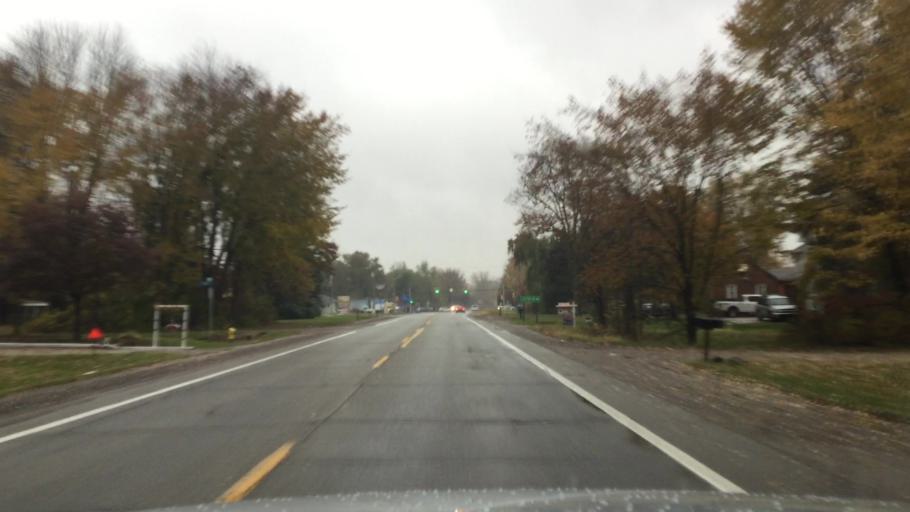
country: US
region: Michigan
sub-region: Macomb County
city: New Baltimore
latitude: 42.6492
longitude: -82.8079
